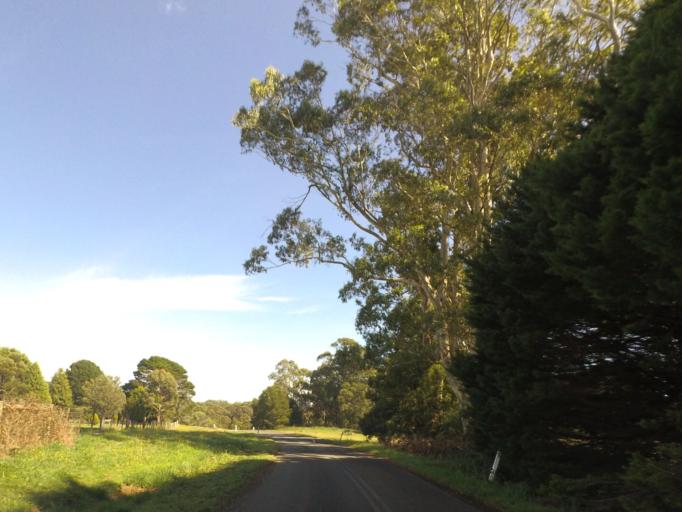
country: AU
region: Victoria
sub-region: Moorabool
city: Bacchus Marsh
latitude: -37.4237
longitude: 144.3824
